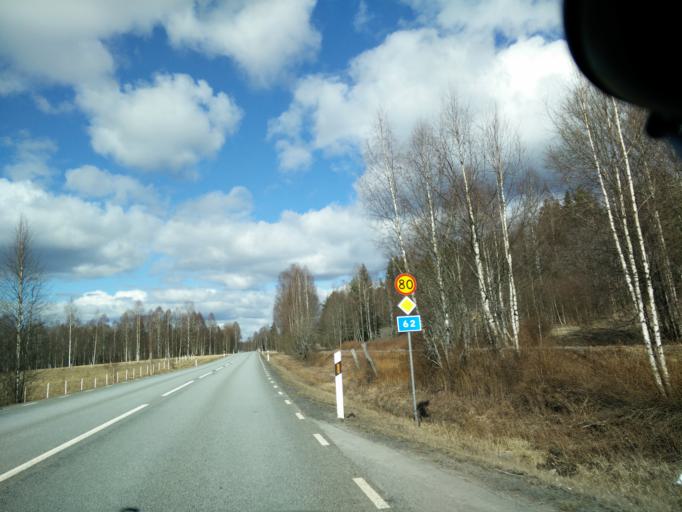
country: SE
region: Vaermland
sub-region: Munkfors Kommun
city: Munkfors
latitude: 59.8615
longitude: 13.5611
